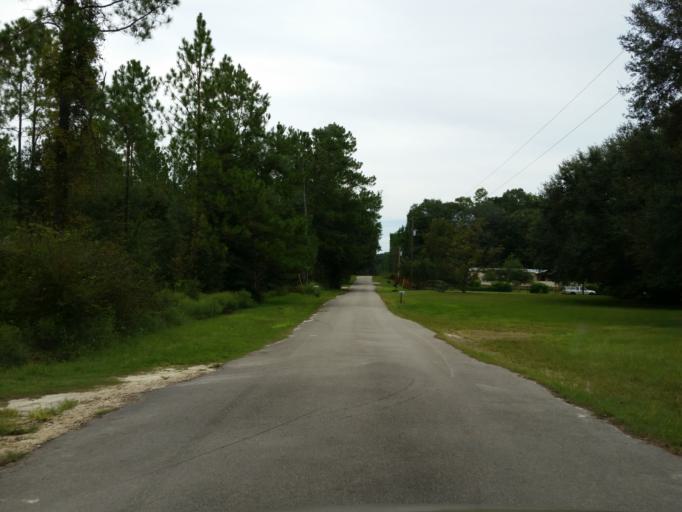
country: US
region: Florida
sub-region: Alachua County
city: High Springs
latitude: 29.9787
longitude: -82.5636
